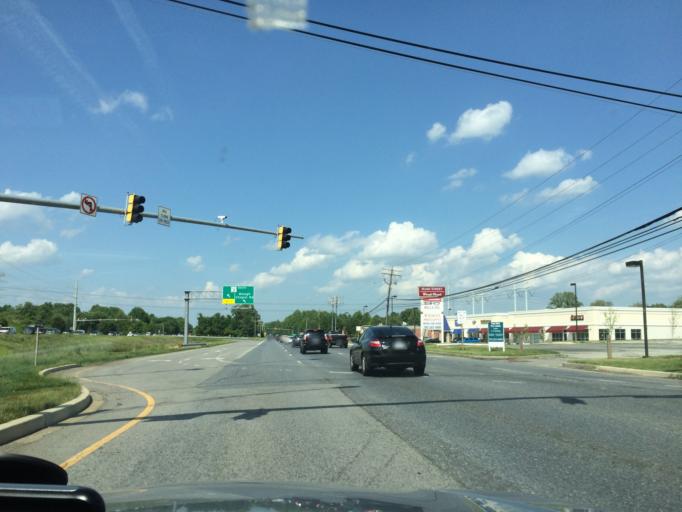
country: US
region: Maryland
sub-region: Anne Arundel County
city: Gambrills
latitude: 39.0390
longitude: -76.6747
